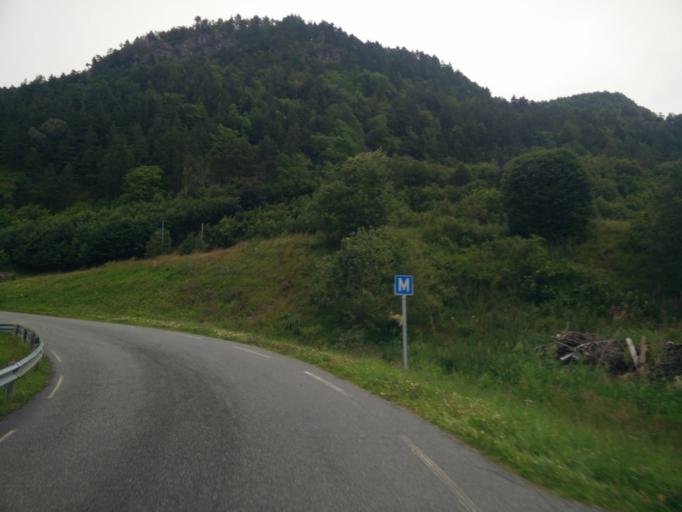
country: NO
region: More og Romsdal
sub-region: Kristiansund
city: Rensvik
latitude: 63.0149
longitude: 7.9114
